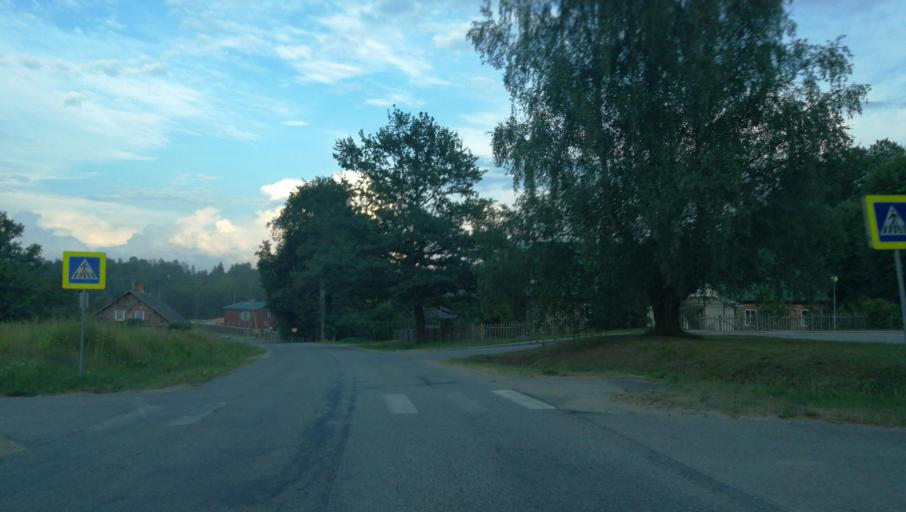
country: LV
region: Priekuli
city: Priekuli
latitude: 57.2750
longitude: 25.3252
